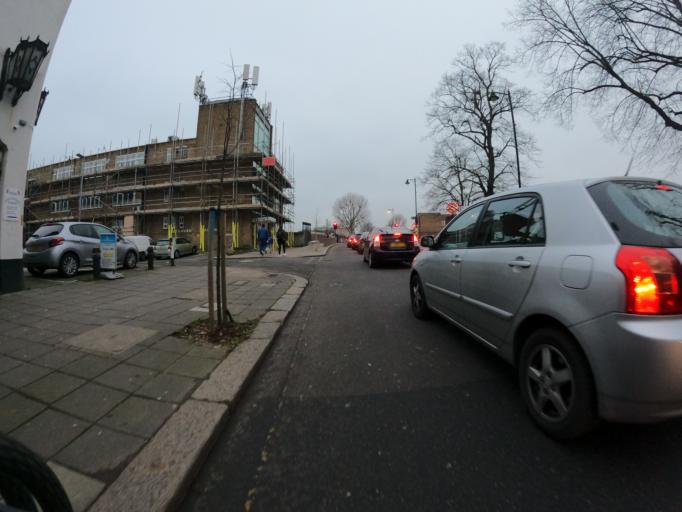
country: GB
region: England
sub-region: Greater London
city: Brentford
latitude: 51.4989
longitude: -0.3144
